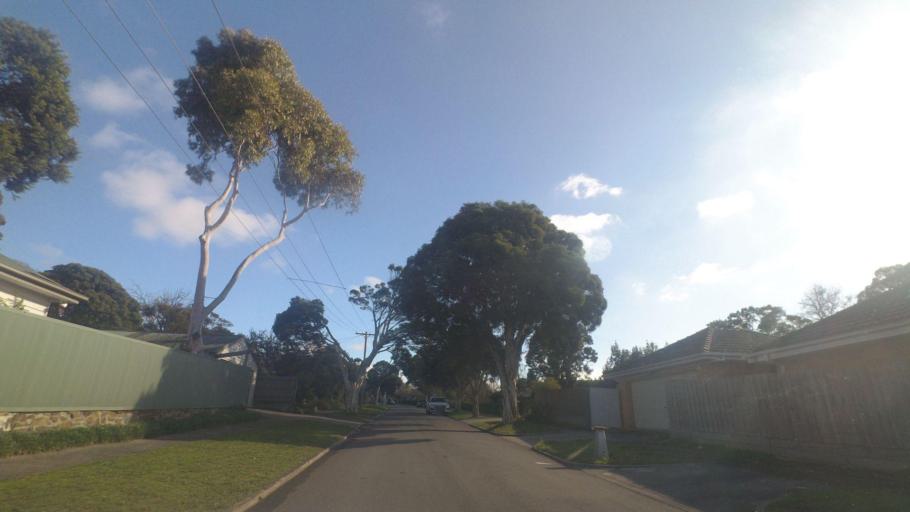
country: AU
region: Victoria
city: Mont Albert
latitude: -37.8086
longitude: 145.1034
